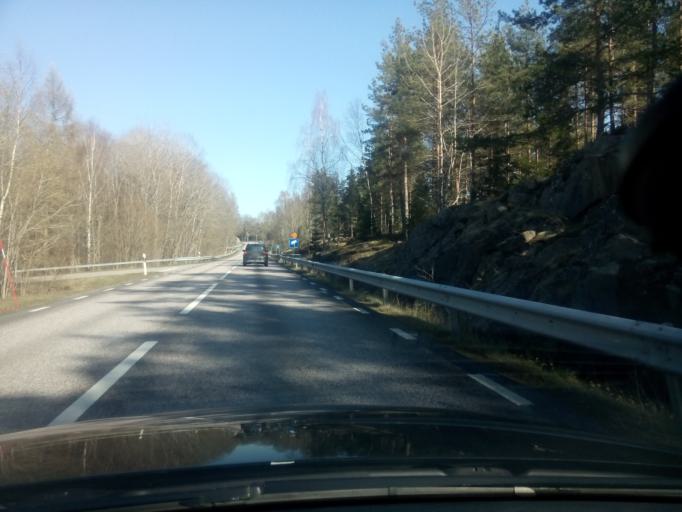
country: SE
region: Soedermanland
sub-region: Flens Kommun
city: Malmkoping
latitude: 59.2048
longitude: 16.8202
